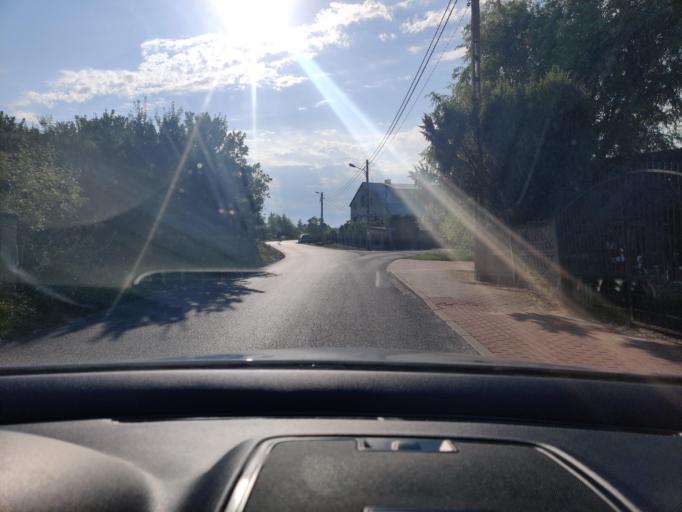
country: PL
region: Greater Poland Voivodeship
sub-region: Konin
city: Konin
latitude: 52.1914
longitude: 18.3166
